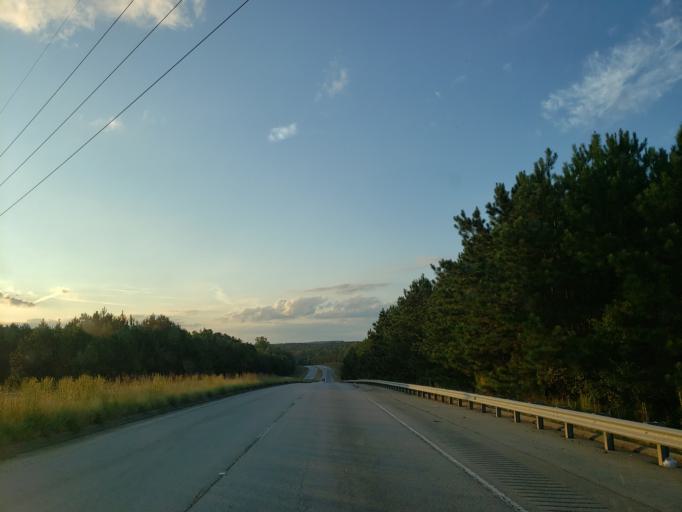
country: US
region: Georgia
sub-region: Carroll County
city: Carrollton
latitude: 33.6078
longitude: -85.0594
